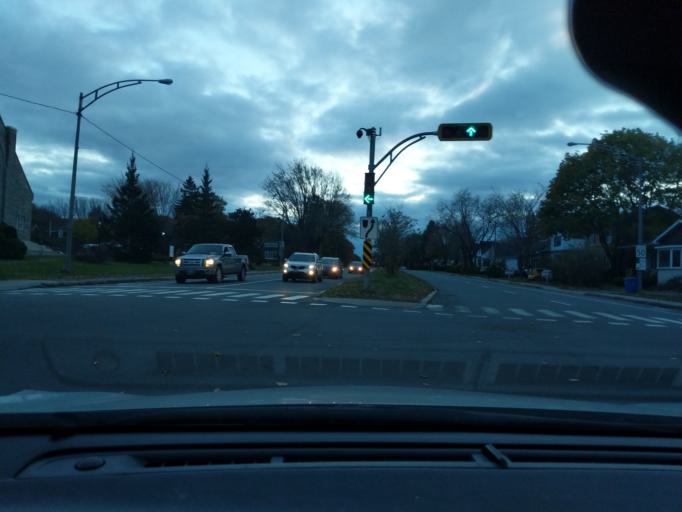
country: CA
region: Quebec
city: Quebec
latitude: 46.7869
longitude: -71.2508
